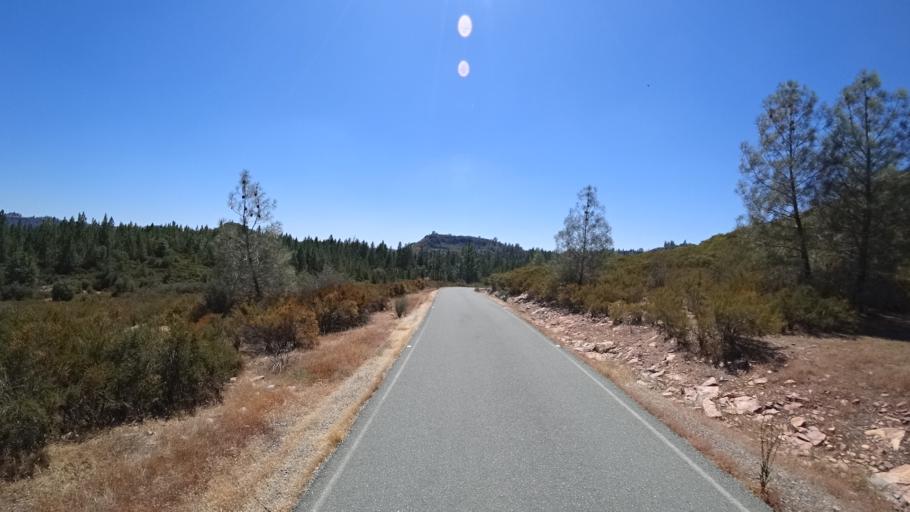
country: US
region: California
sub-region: Calaveras County
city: Mountain Ranch
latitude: 38.2895
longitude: -120.4871
